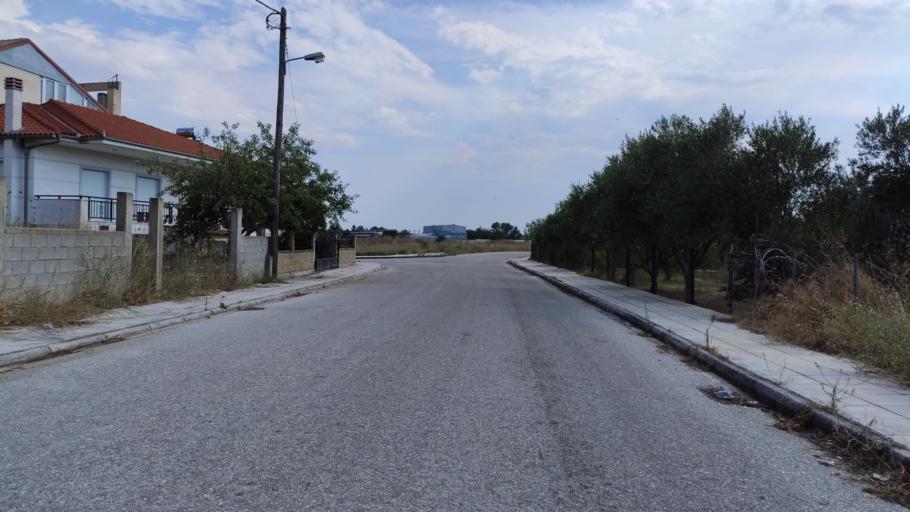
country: GR
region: East Macedonia and Thrace
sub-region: Nomos Rodopis
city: Komotini
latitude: 41.1313
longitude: 25.3908
